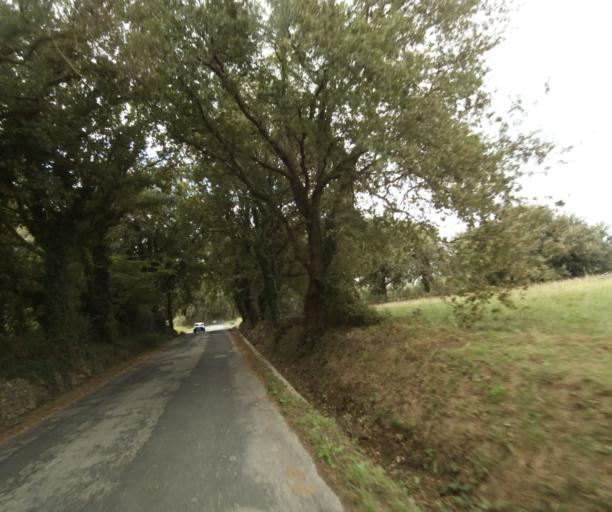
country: FR
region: Languedoc-Roussillon
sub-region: Departement des Pyrenees-Orientales
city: Argelers
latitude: 42.5626
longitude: 3.0285
